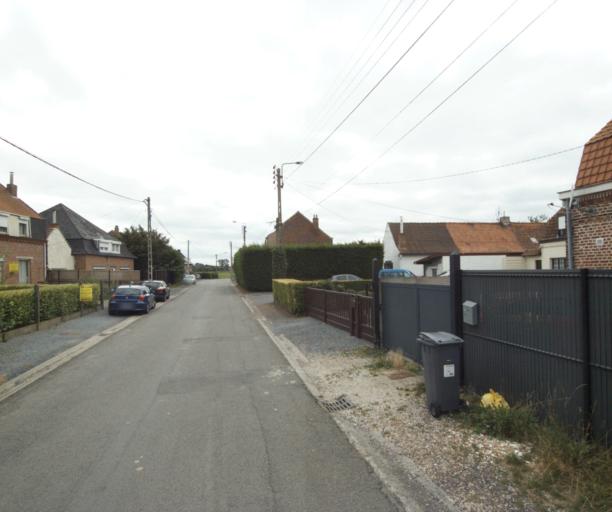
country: FR
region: Nord-Pas-de-Calais
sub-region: Departement du Nord
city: Leers
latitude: 50.6720
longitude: 3.2484
